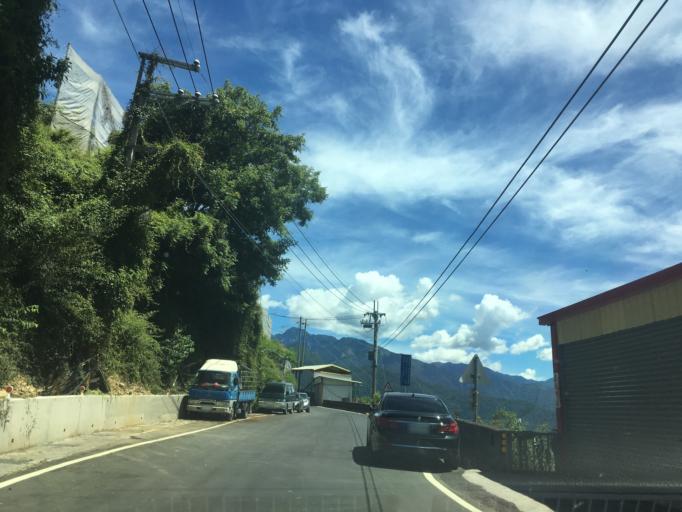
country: TW
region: Taiwan
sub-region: Nantou
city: Puli
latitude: 24.2569
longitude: 121.2638
